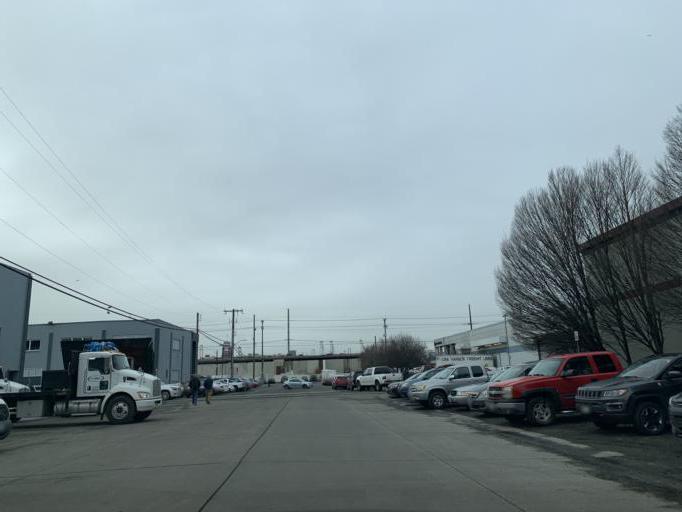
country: US
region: Washington
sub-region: King County
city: Seattle
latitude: 47.5819
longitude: -122.3241
